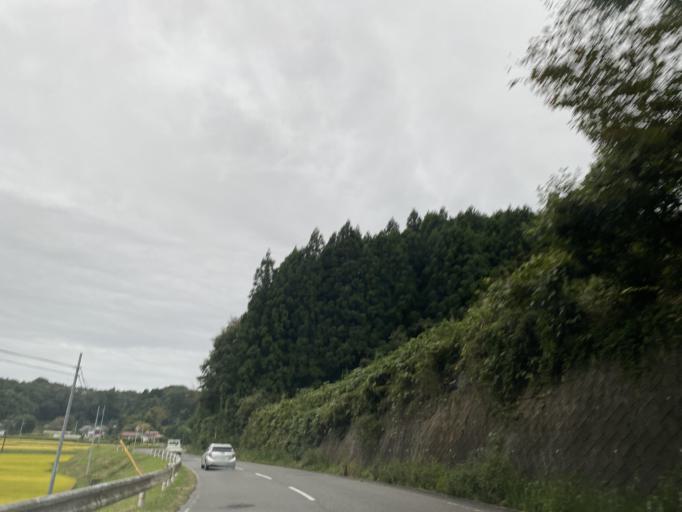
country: JP
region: Fukushima
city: Sukagawa
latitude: 37.3074
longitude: 140.2628
